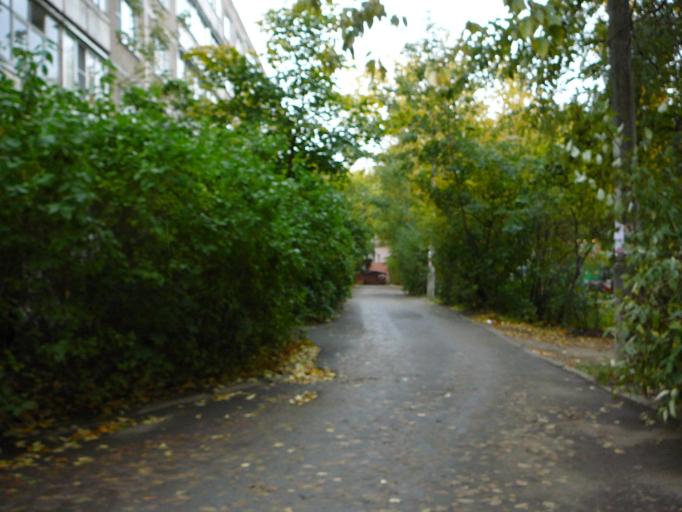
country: RU
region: Moskovskaya
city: Yegor'yevsk
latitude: 55.3896
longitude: 39.0283
